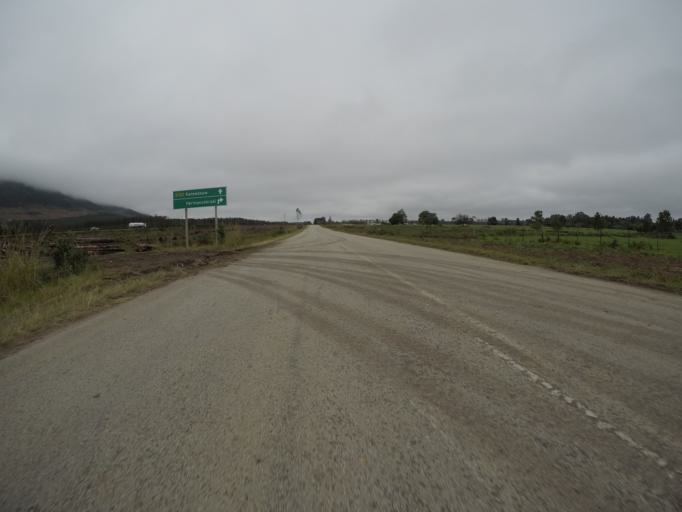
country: ZA
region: Eastern Cape
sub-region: Cacadu District Municipality
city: Kareedouw
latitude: -33.9860
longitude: 24.0673
